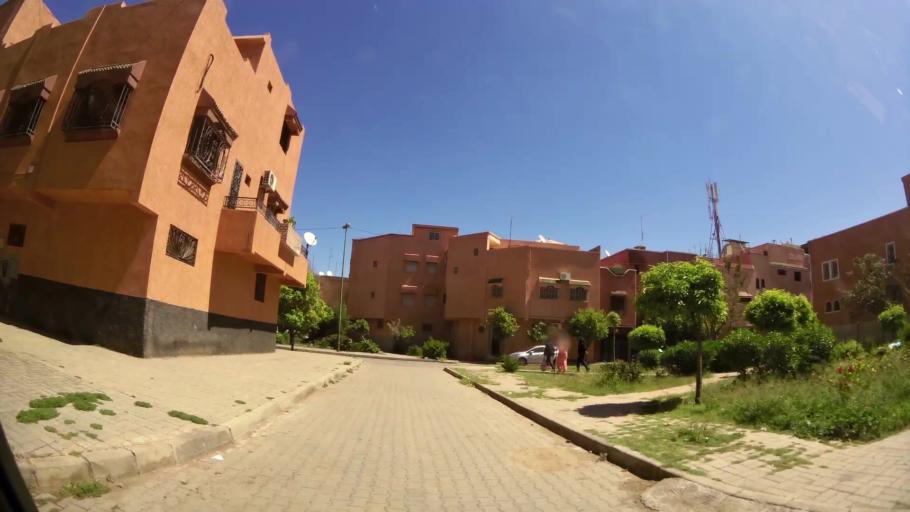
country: MA
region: Marrakech-Tensift-Al Haouz
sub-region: Marrakech
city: Marrakesh
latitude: 31.6577
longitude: -7.9901
